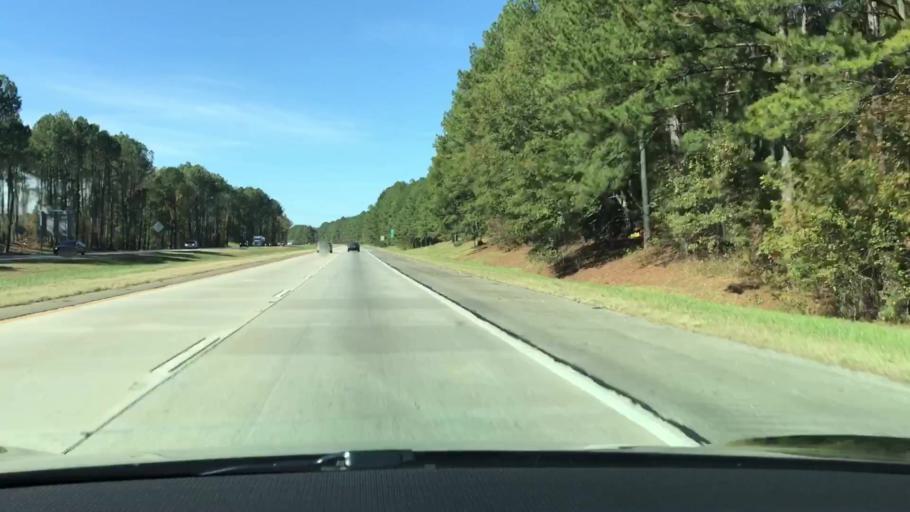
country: US
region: Georgia
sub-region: Taliaferro County
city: Crawfordville
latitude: 33.5304
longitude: -82.9213
